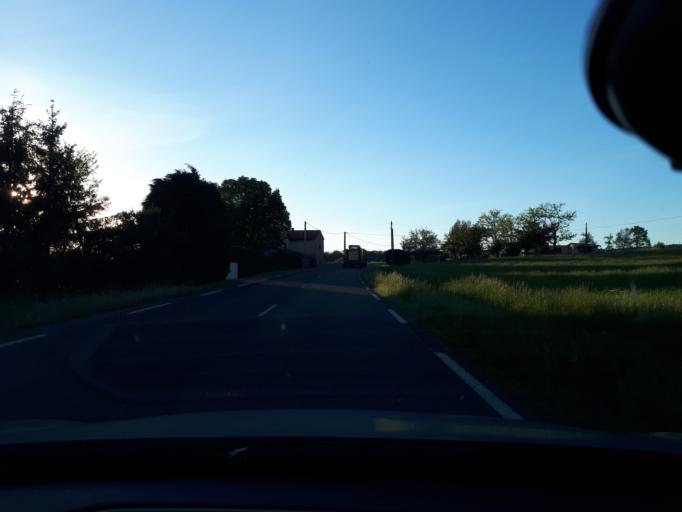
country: FR
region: Rhone-Alpes
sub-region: Departement de la Loire
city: Civens
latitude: 45.7501
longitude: 4.2720
